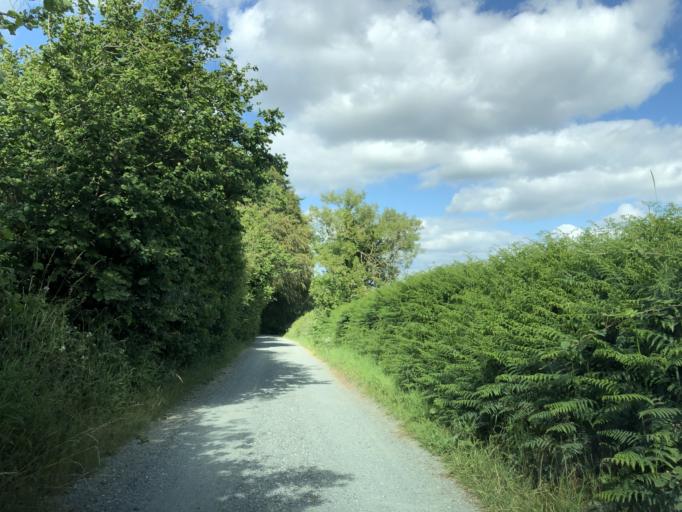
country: DK
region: South Denmark
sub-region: Vejle Kommune
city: Brejning
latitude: 55.6763
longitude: 9.6563
